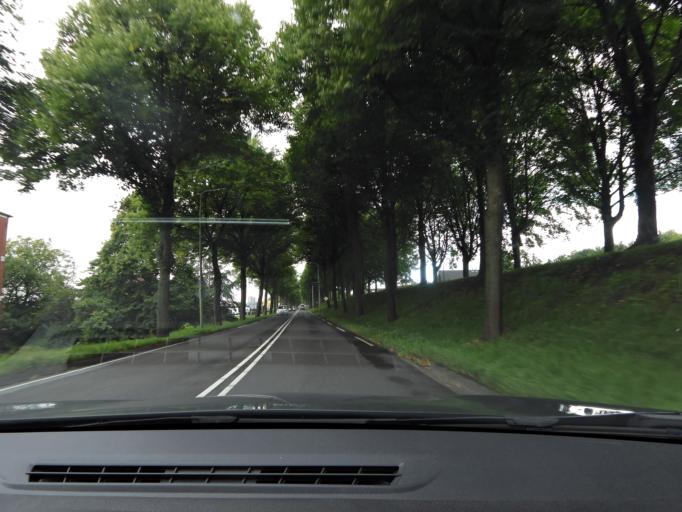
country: NL
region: South Holland
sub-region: Gemeente Oud-Beijerland
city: Oud-Beijerland
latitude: 51.8214
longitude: 4.4357
